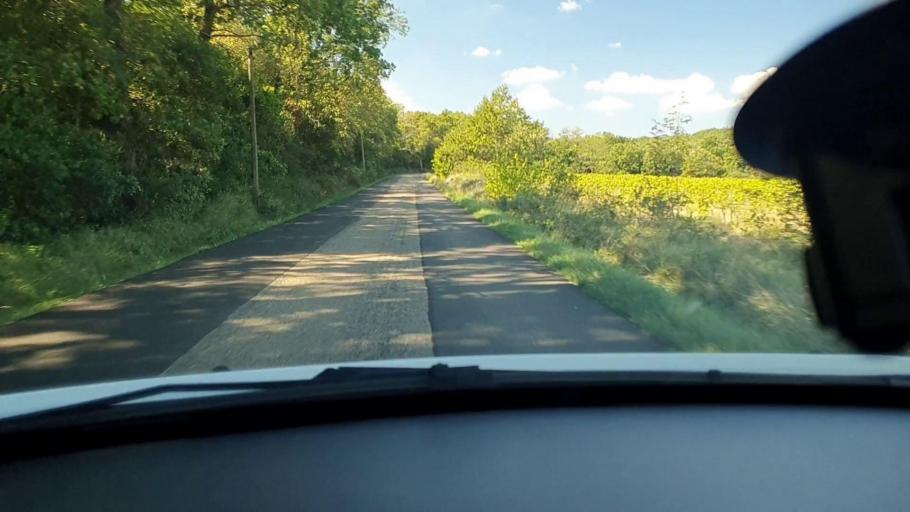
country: FR
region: Languedoc-Roussillon
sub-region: Departement du Gard
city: Sabran
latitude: 44.1747
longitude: 4.5151
